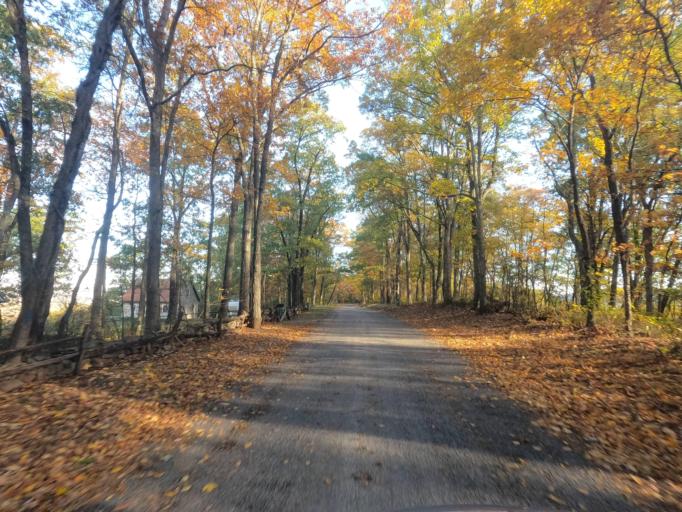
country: US
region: West Virginia
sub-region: Morgan County
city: Berkeley Springs
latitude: 39.6069
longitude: -78.4947
